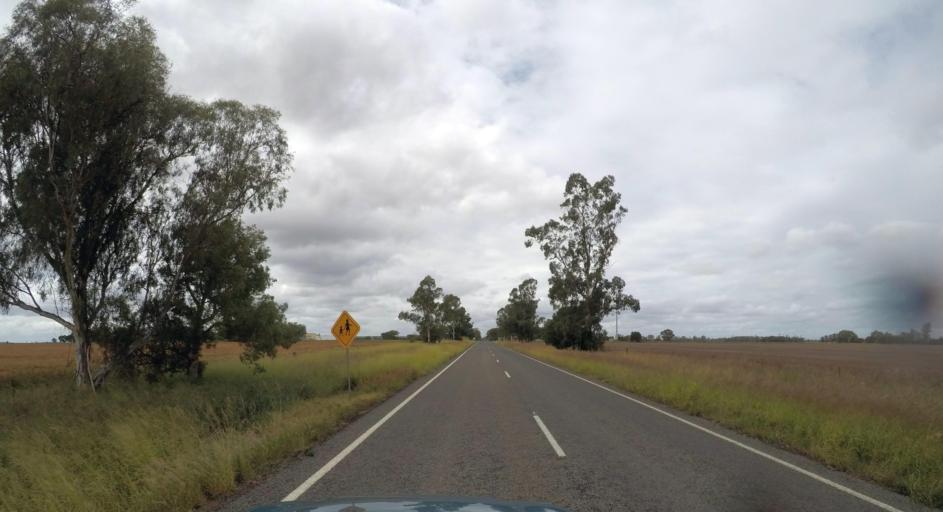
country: AU
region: Queensland
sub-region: South Burnett
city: Kingaroy
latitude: -26.3948
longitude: 151.2405
